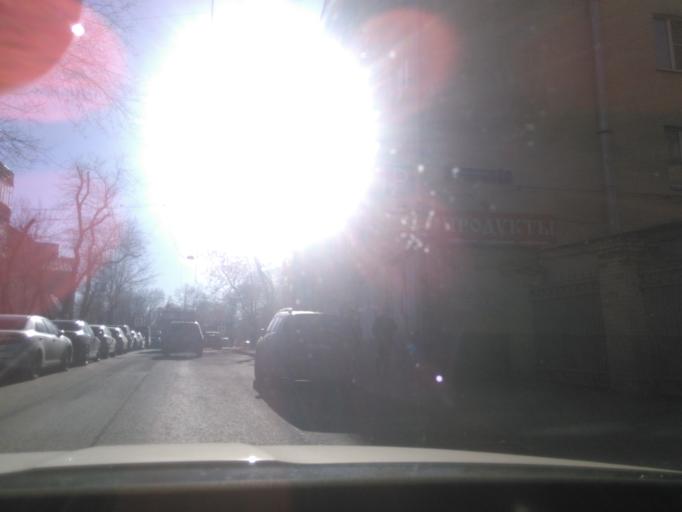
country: RU
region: Moskovskaya
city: Dorogomilovo
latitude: 55.7359
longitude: 37.5723
